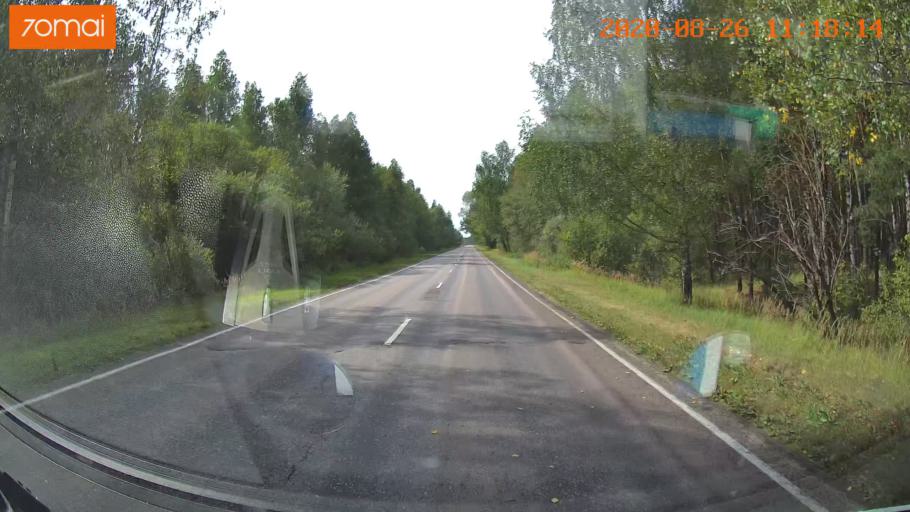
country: RU
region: Rjazan
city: Shilovo
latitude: 54.4119
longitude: 41.1006
